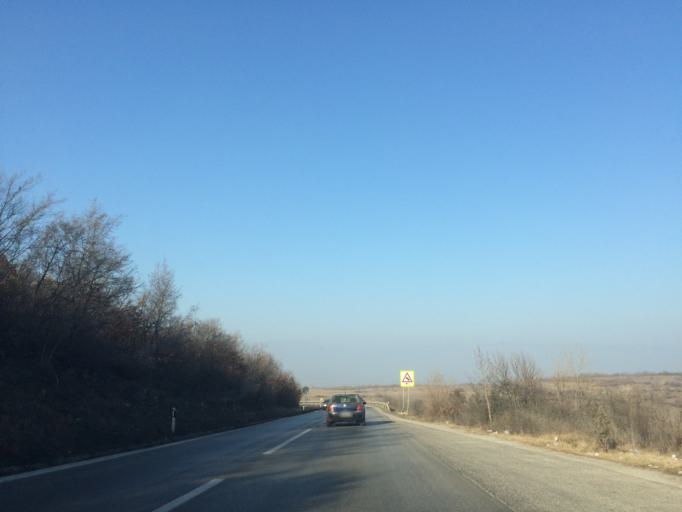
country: XK
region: Pec
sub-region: Komuna e Klines
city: Klina
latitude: 42.5960
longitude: 20.6102
